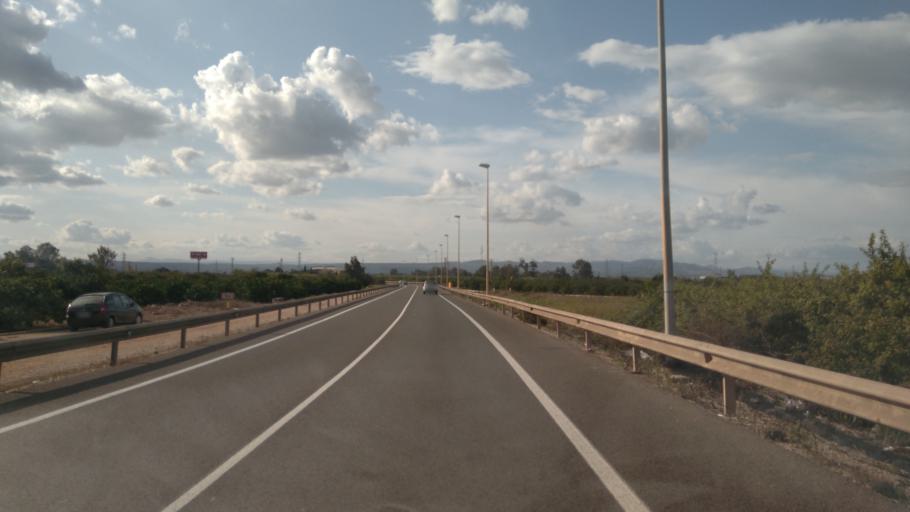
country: ES
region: Valencia
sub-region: Provincia de Valencia
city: Alzira
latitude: 39.1634
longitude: -0.4387
